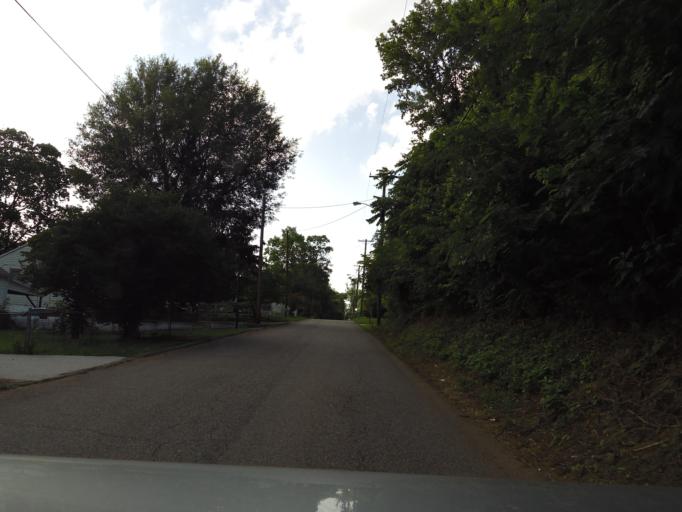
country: US
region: Tennessee
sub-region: Knox County
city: Knoxville
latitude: 35.9515
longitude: -83.8793
